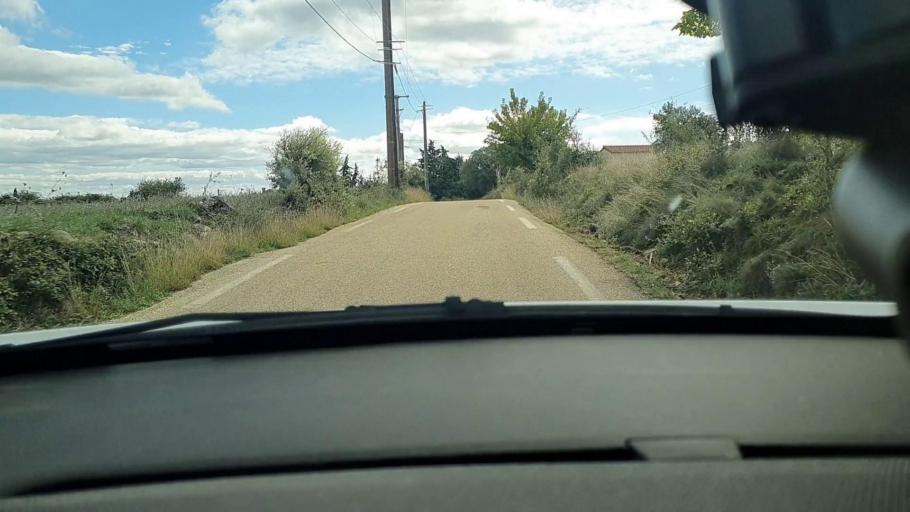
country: FR
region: Languedoc-Roussillon
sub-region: Departement du Gard
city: Besseges
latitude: 44.3088
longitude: 4.0249
